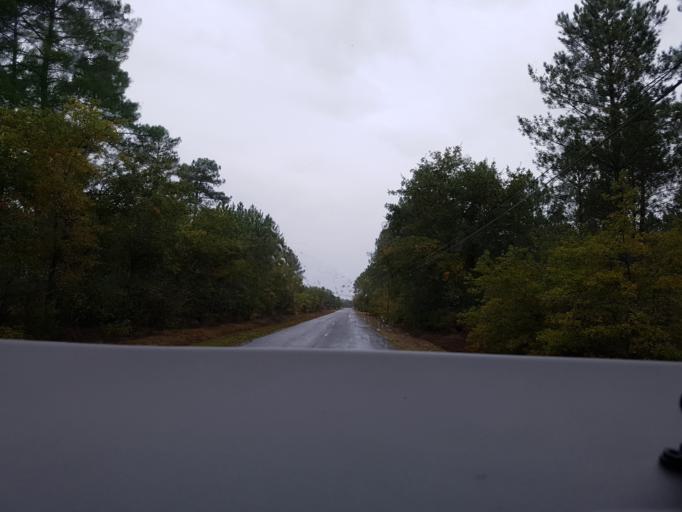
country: FR
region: Aquitaine
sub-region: Departement de la Gironde
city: Saint-Symphorien
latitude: 44.3520
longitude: -0.6219
